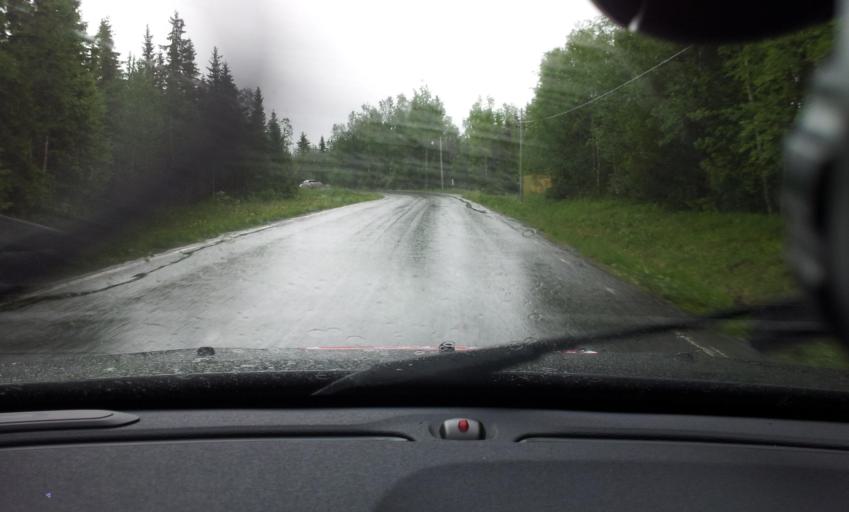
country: SE
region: Jaemtland
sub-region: Are Kommun
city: Are
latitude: 63.3107
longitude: 13.2228
